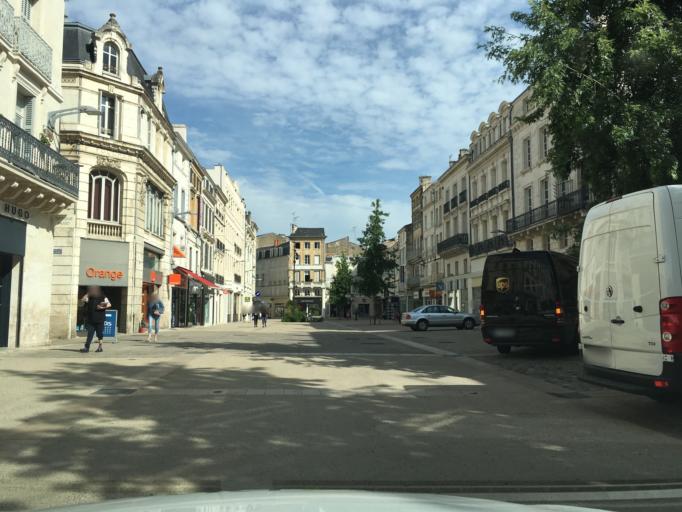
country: FR
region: Poitou-Charentes
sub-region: Departement des Deux-Sevres
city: Niort
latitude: 46.3246
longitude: -0.4620
